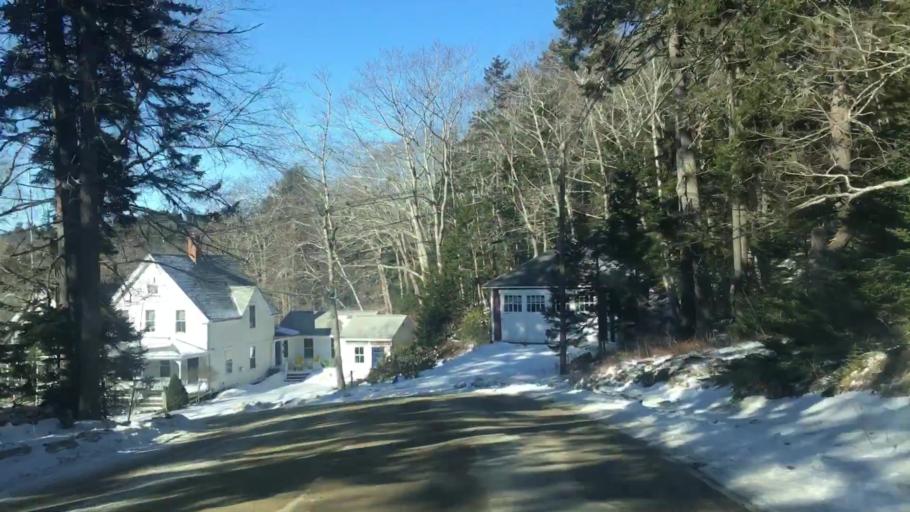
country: US
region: Maine
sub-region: Hancock County
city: Castine
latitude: 44.3412
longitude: -68.7351
